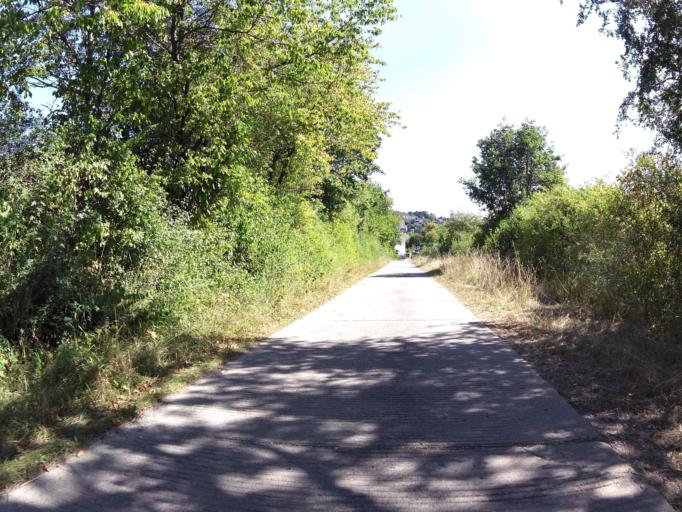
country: DE
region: Bavaria
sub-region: Regierungsbezirk Unterfranken
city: Guntersleben
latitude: 49.8657
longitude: 9.8973
